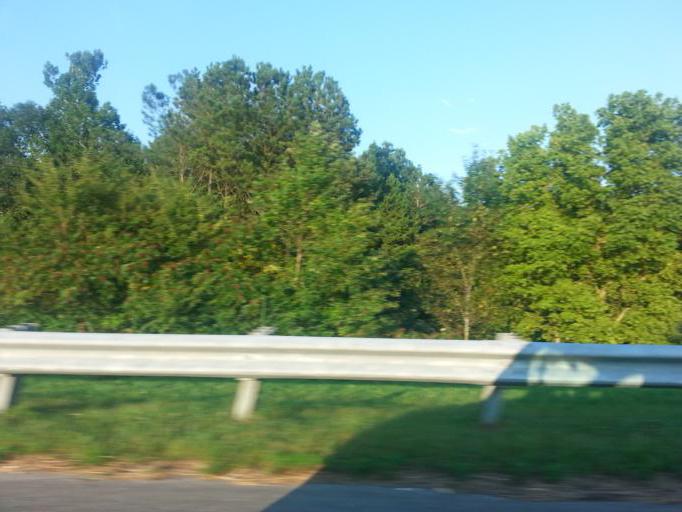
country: US
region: Tennessee
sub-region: Meigs County
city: Decatur
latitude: 35.5557
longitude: -84.6676
